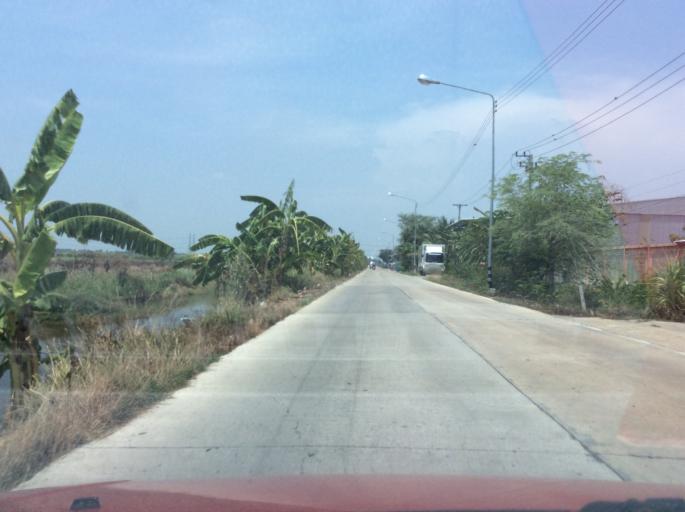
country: TH
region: Pathum Thani
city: Ban Lam Luk Ka
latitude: 13.9844
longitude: 100.7575
